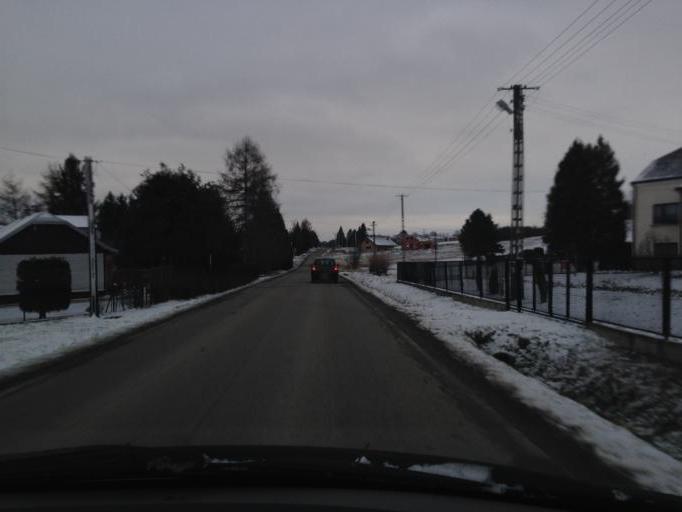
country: PL
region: Lesser Poland Voivodeship
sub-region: Powiat gorlicki
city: Moszczenica
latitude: 49.7139
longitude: 21.1127
